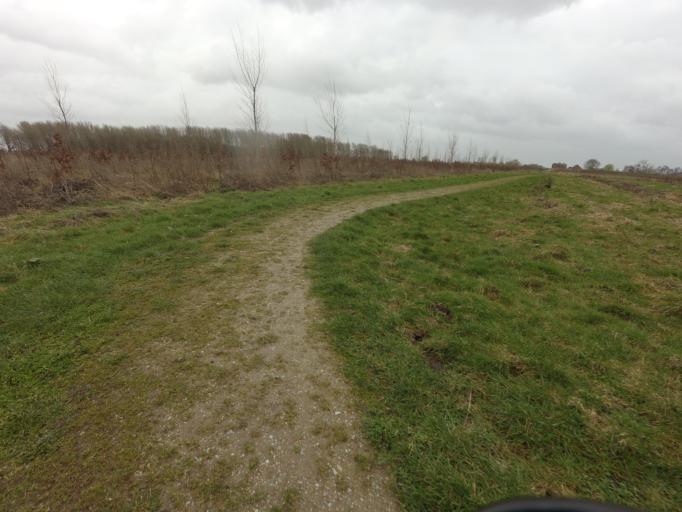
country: NL
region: Utrecht
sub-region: Gemeente IJsselstein
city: IJsselstein
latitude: 52.0457
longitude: 5.0349
